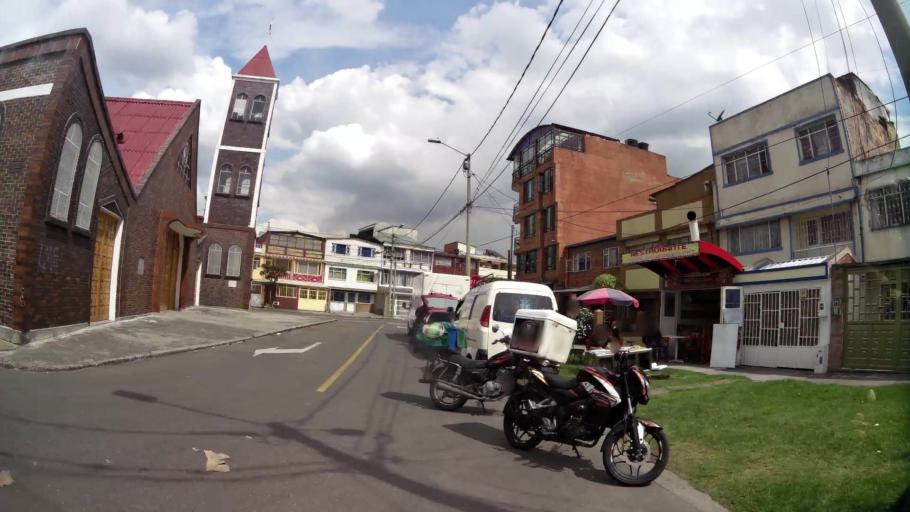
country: CO
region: Bogota D.C.
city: Bogota
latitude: 4.6109
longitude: -74.1152
